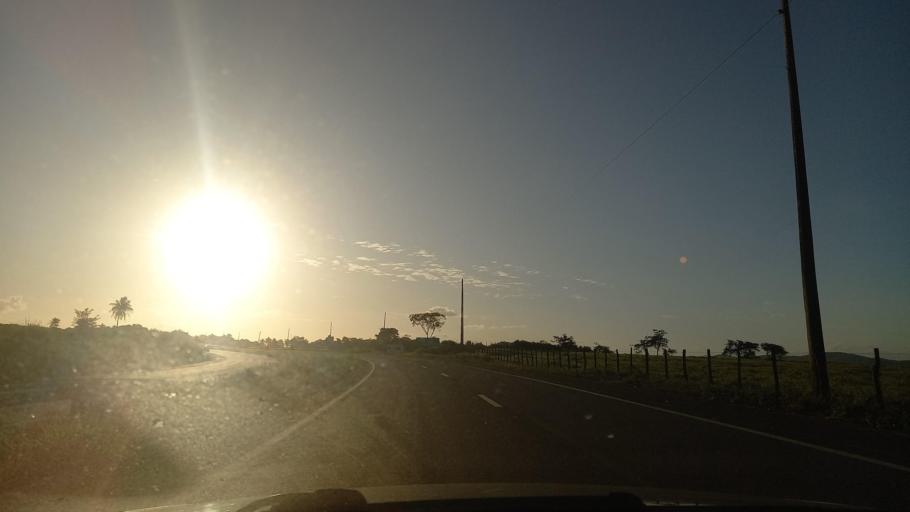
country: BR
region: Alagoas
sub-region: Limoeiro De Anadia
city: Limoeiro de Anadia
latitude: -9.7591
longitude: -36.5141
